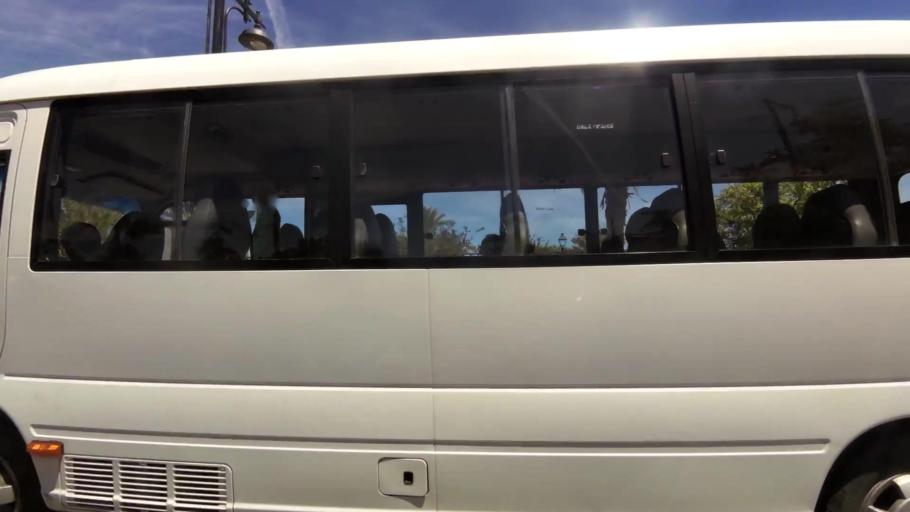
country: MA
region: Marrakech-Tensift-Al Haouz
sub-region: Marrakech
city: Marrakesh
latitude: 31.6223
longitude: -7.9964
